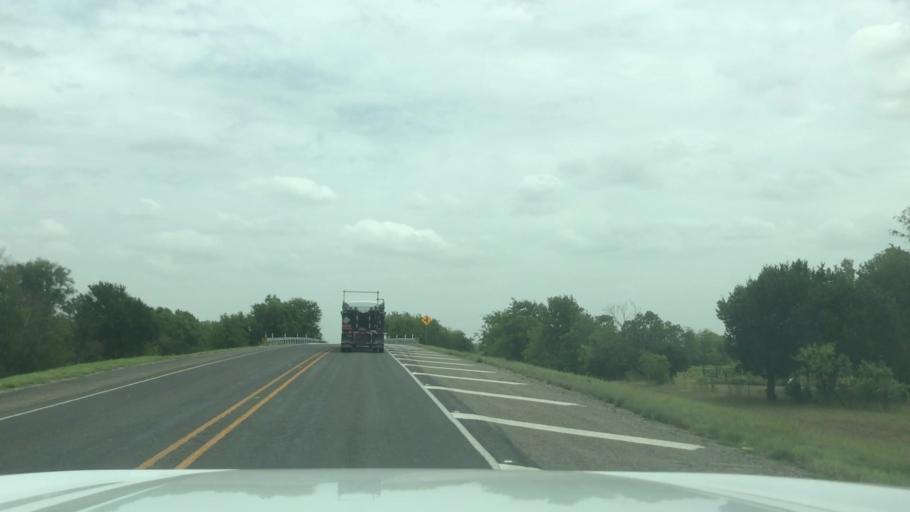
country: US
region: Texas
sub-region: Bosque County
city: Valley Mills
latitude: 31.6751
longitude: -97.5154
